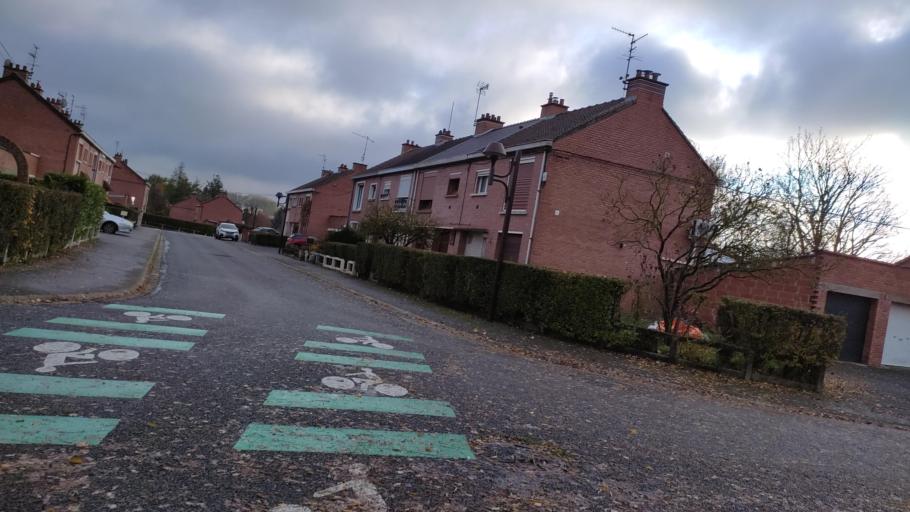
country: FR
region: Nord-Pas-de-Calais
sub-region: Departement du Pas-de-Calais
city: Dainville
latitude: 50.2861
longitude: 2.7327
